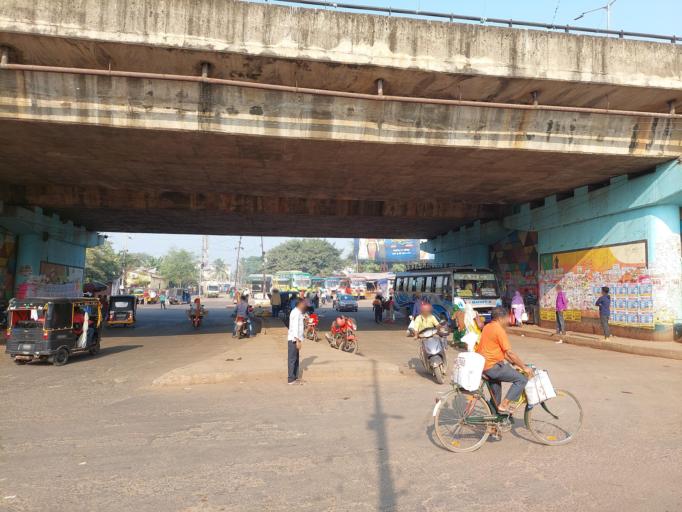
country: IN
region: Odisha
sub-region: Khordha
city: Bhubaneshwar
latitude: 20.2715
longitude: 85.7940
